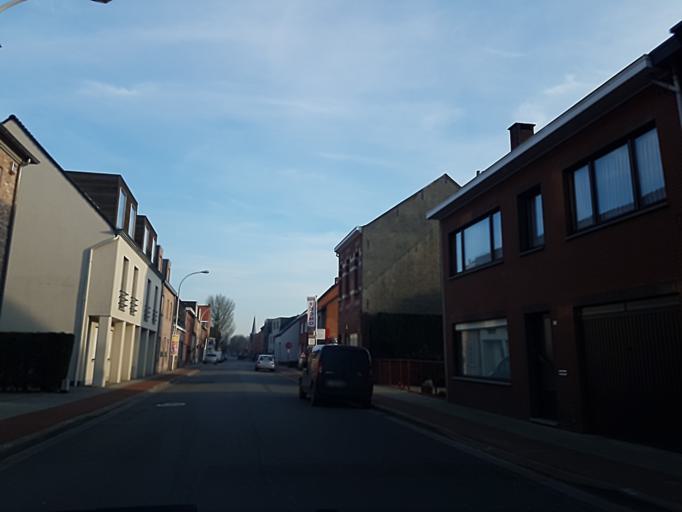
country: BE
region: Flanders
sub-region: Provincie Antwerpen
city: Zandhoven
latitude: 51.2407
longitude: 4.6413
